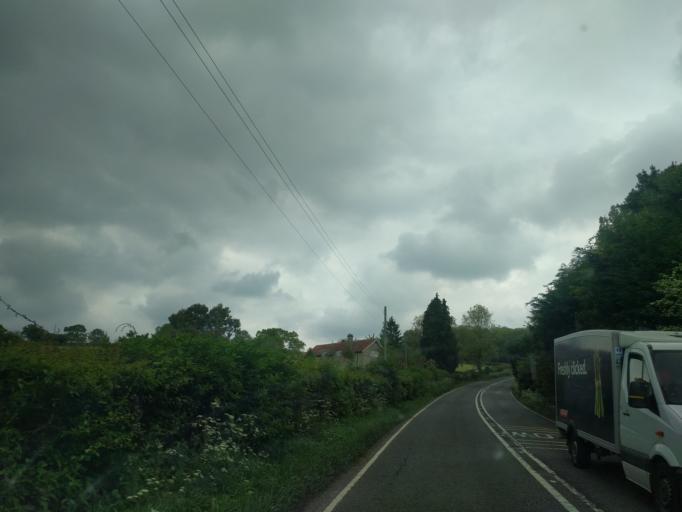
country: GB
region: England
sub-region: Somerset
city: Castle Cary
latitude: 51.1265
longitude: -2.5704
